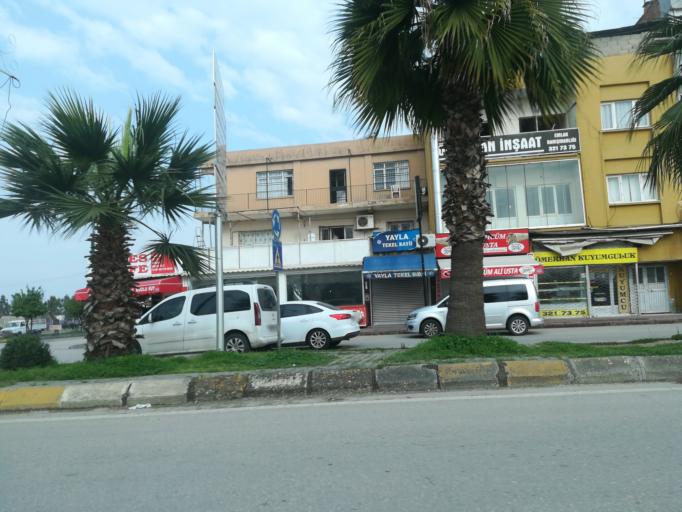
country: TR
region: Adana
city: Yuregir
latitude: 36.9974
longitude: 35.3585
